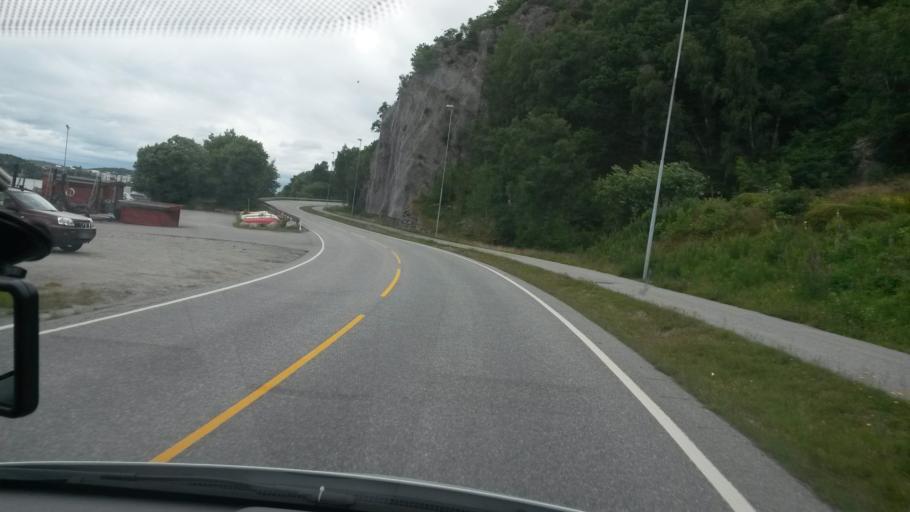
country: NO
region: Rogaland
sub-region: Sandnes
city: Sandnes
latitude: 58.8716
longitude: 5.7658
